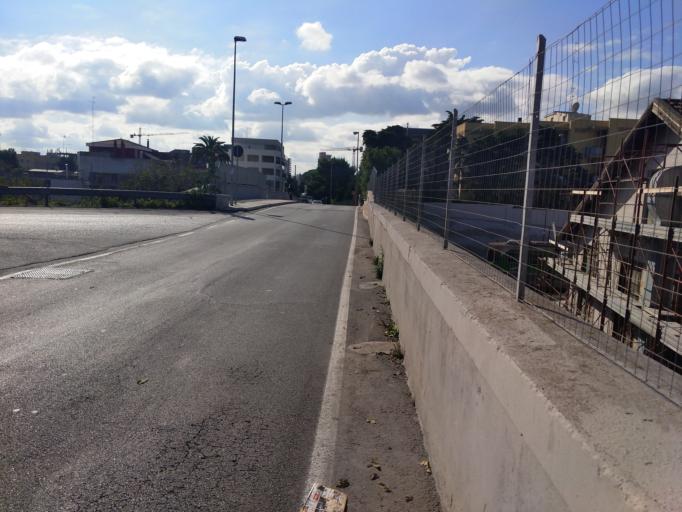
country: IT
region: Apulia
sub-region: Provincia di Bari
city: Bari
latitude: 41.1139
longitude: 16.8564
